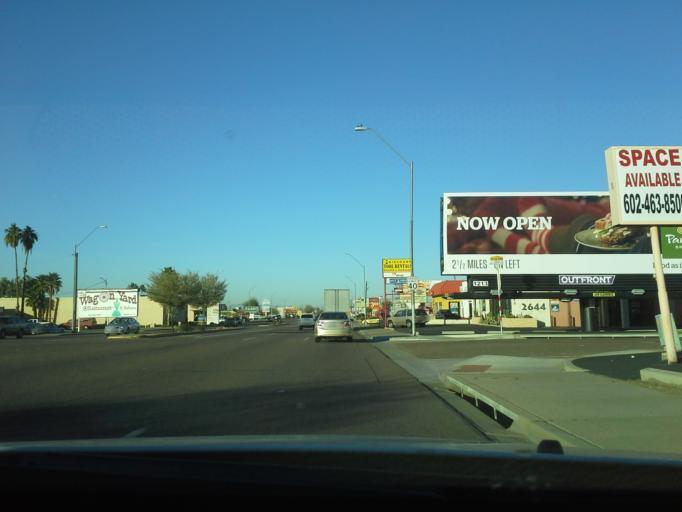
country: US
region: Arizona
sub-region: Maricopa County
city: Paradise Valley
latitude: 33.6407
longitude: -112.0241
